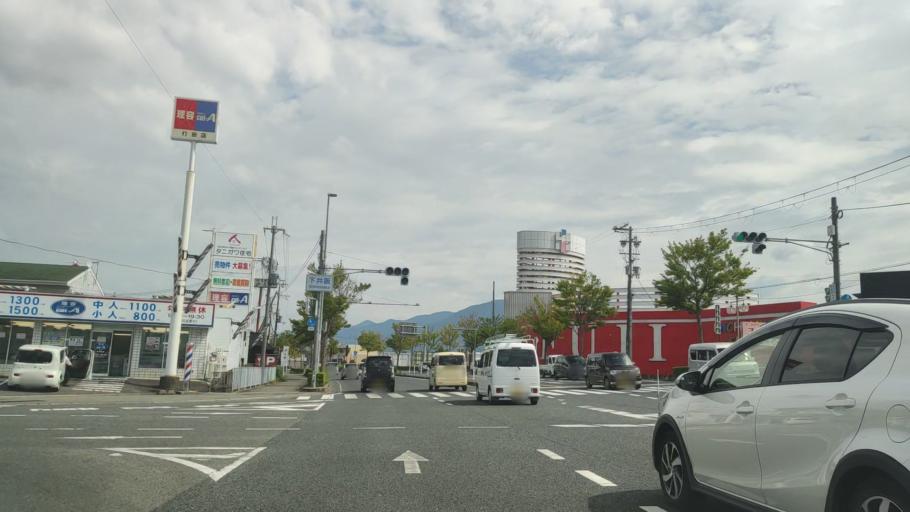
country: JP
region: Wakayama
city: Iwade
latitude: 34.2600
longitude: 135.3413
